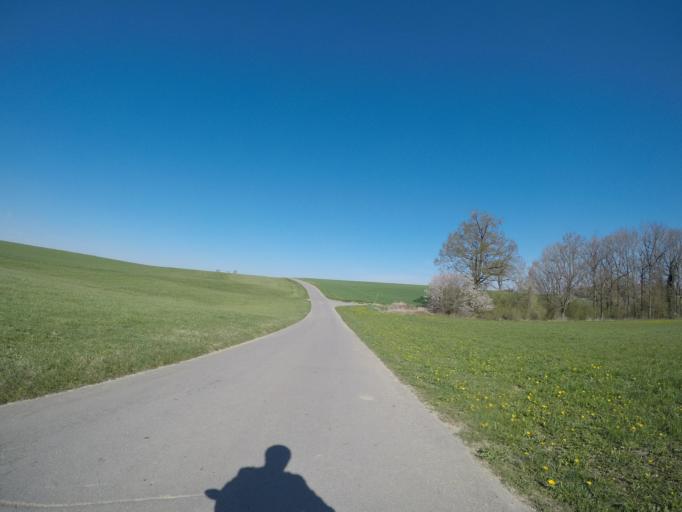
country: DE
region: Baden-Wuerttemberg
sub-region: Tuebingen Region
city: Fleischwangen
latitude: 47.8726
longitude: 9.5042
